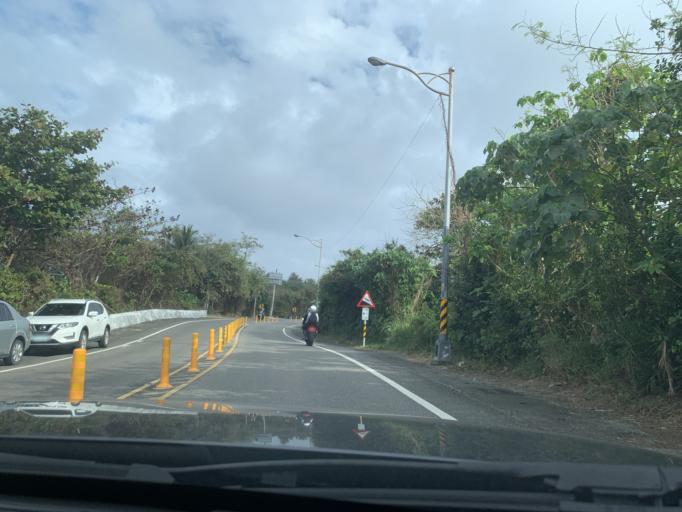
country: TW
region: Taiwan
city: Hengchun
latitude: 21.9051
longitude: 120.8521
